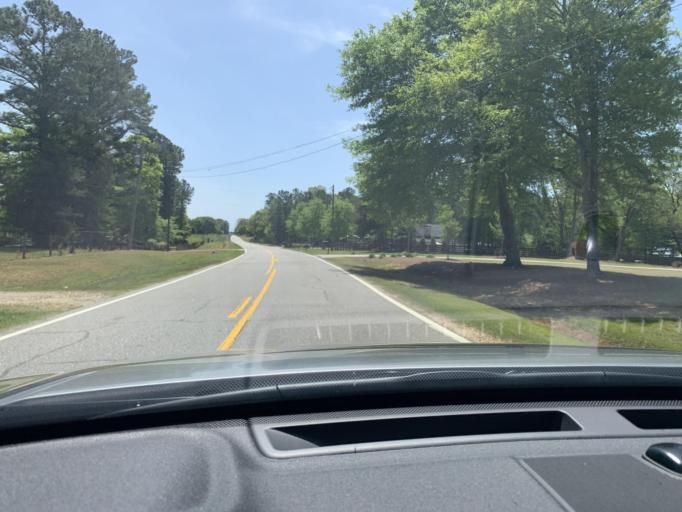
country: US
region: Georgia
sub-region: Oconee County
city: Bogart
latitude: 33.8652
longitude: -83.5532
